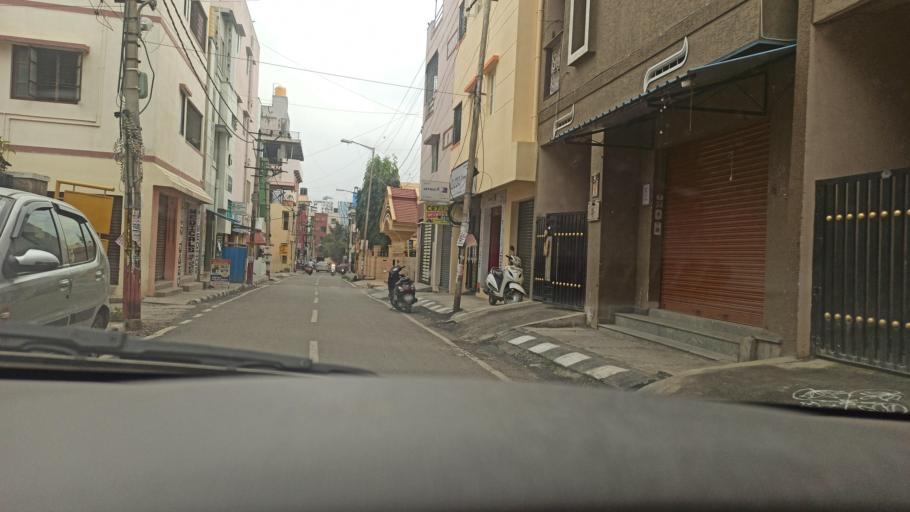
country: IN
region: Karnataka
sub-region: Bangalore Urban
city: Bangalore
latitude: 12.9947
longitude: 77.6801
